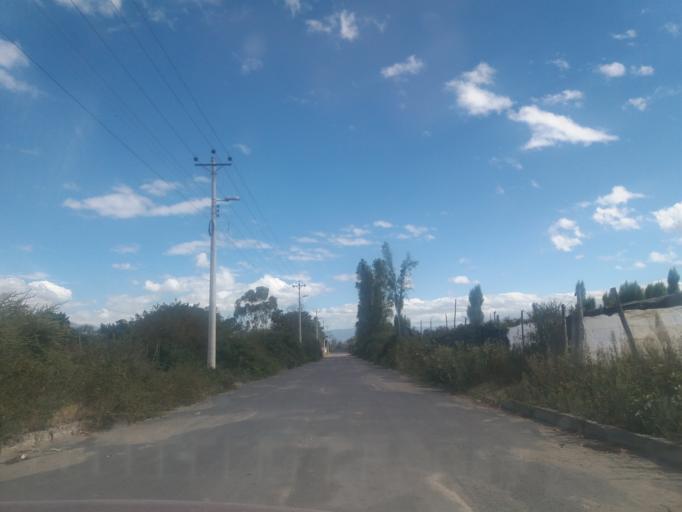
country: EC
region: Pichincha
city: Quito
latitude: -0.1743
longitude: -78.3386
